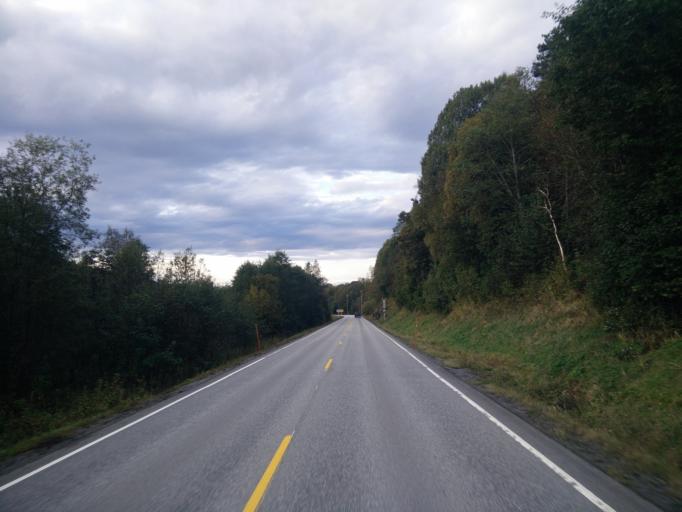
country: NO
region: More og Romsdal
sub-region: Molde
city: Hjelset
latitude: 62.7894
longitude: 7.5248
